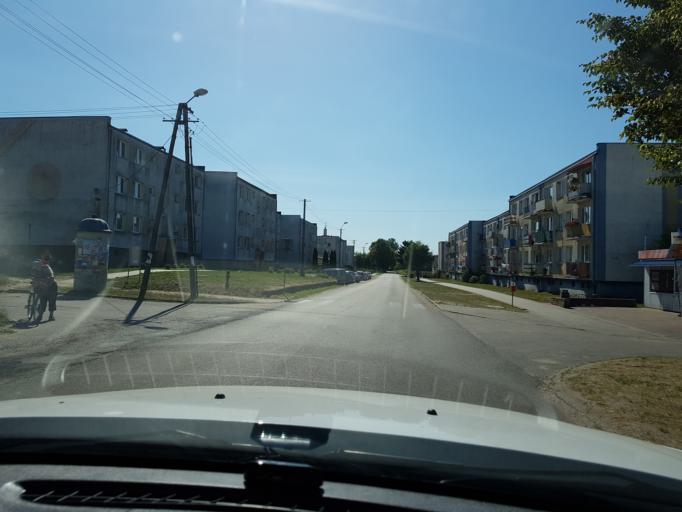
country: PL
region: West Pomeranian Voivodeship
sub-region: Powiat bialogardzki
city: Karlino
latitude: 53.9580
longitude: 15.8967
